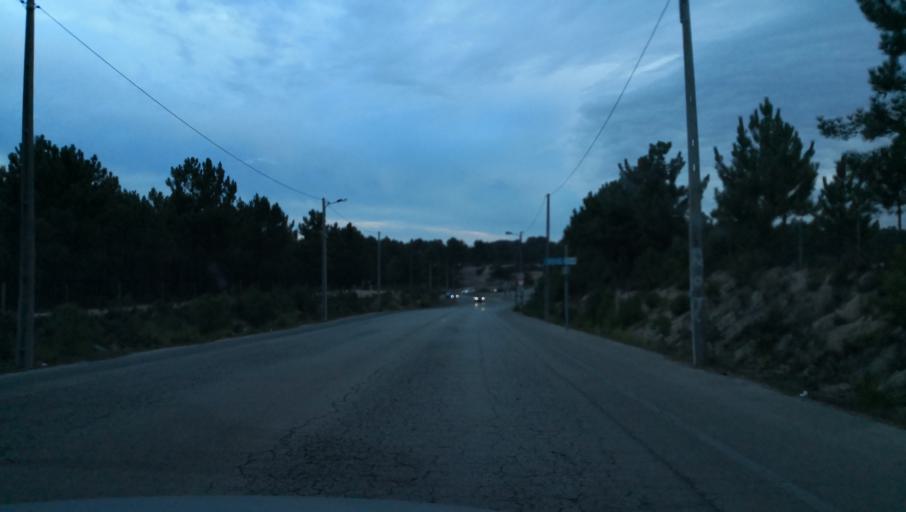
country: PT
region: Setubal
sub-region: Almada
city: Charneca
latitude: 38.5964
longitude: -9.1600
